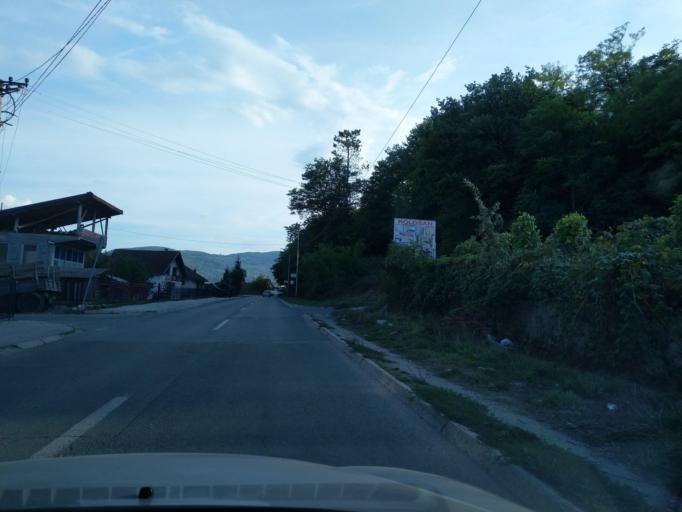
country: RS
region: Central Serbia
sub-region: Zlatiborski Okrug
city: Prijepolje
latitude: 43.3578
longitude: 19.6353
